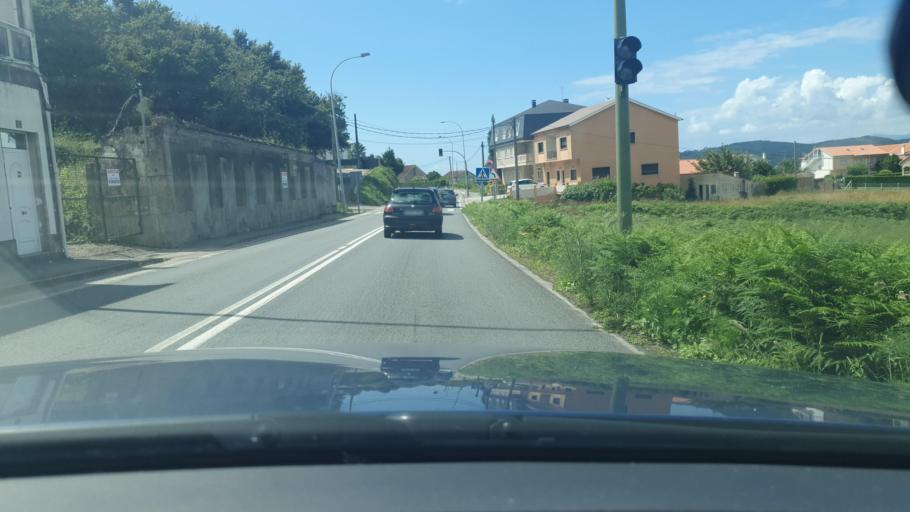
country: ES
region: Galicia
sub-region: Provincia de Pontevedra
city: Sanxenxo
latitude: 42.4403
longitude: -8.8439
